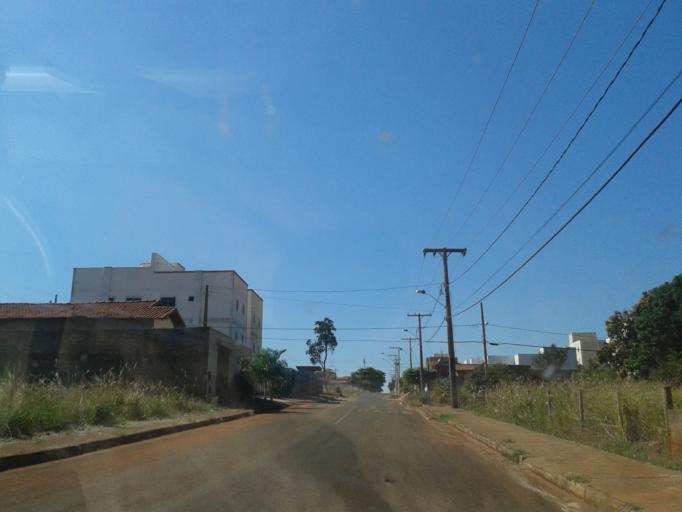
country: BR
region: Minas Gerais
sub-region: Ituiutaba
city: Ituiutaba
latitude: -18.9972
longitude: -49.4583
